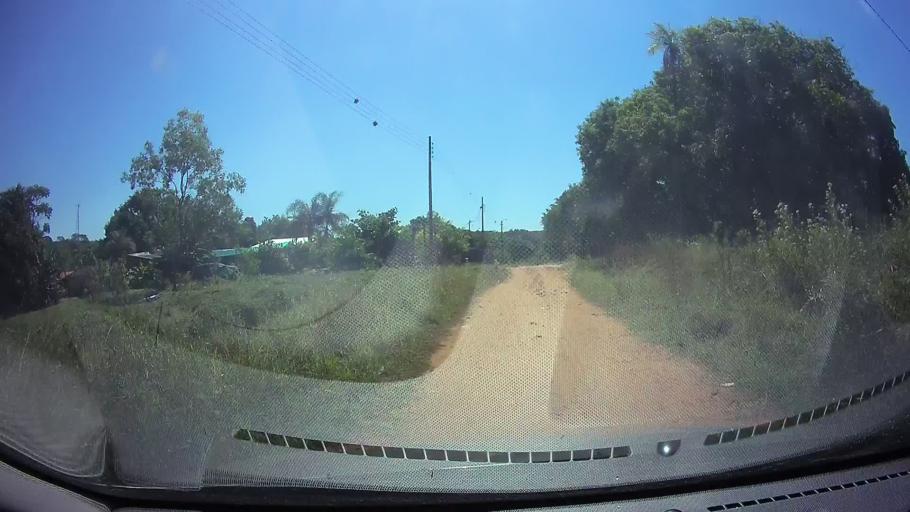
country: PY
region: Central
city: Limpio
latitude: -25.2377
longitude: -57.4506
